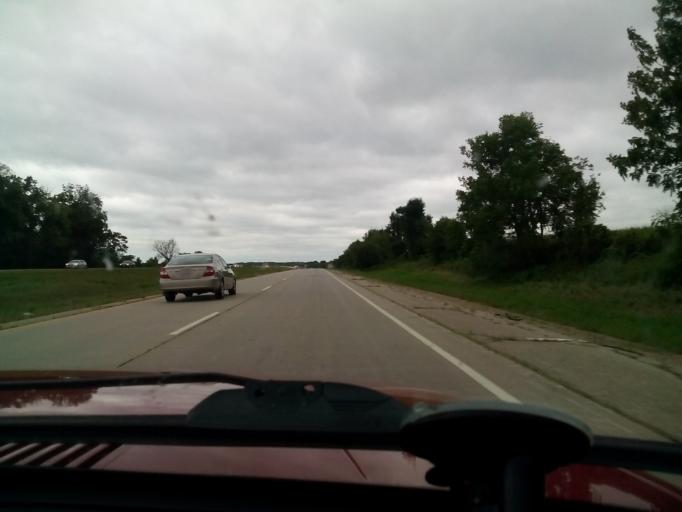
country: US
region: Wisconsin
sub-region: Dane County
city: Sun Prairie
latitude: 43.2495
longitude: -89.1344
